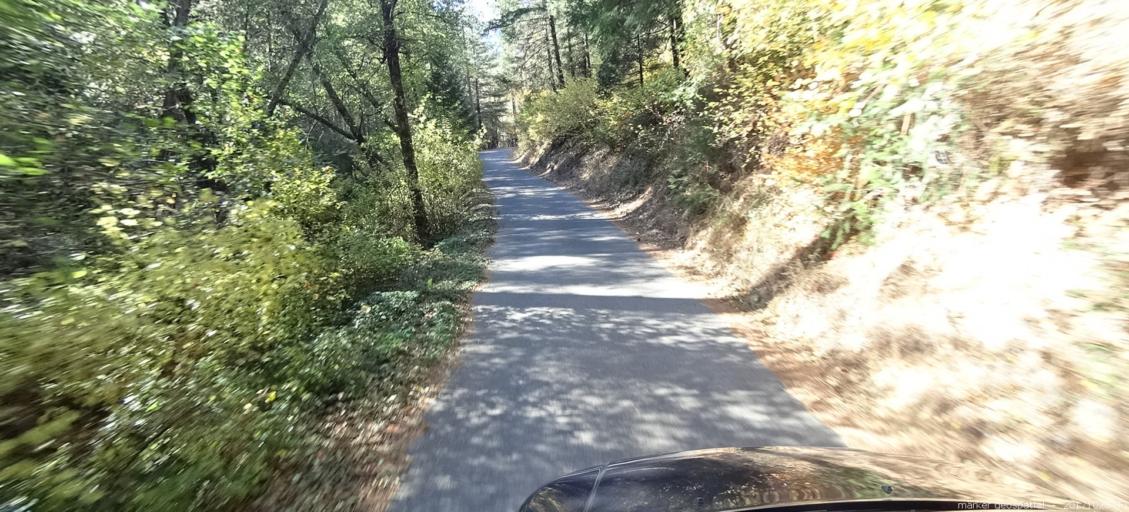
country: US
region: California
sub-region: Shasta County
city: Shasta
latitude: 40.7616
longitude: -122.5691
